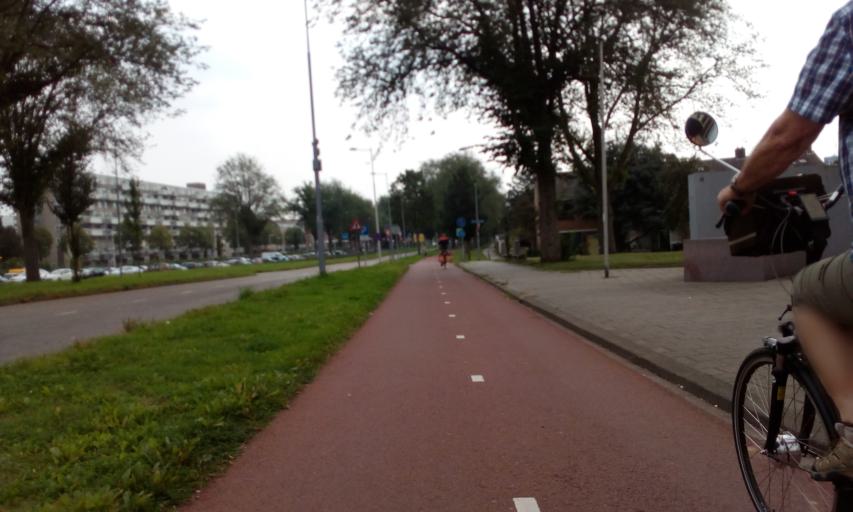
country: NL
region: South Holland
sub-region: Gemeente Rotterdam
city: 's-Gravenland
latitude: 51.9487
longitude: 4.5522
